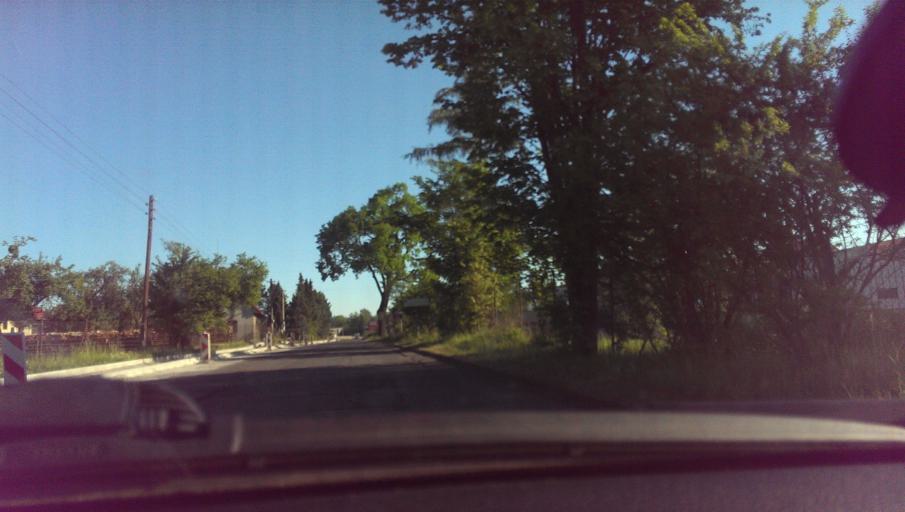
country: CZ
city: Frydlant nad Ostravici
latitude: 49.5776
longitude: 18.3588
